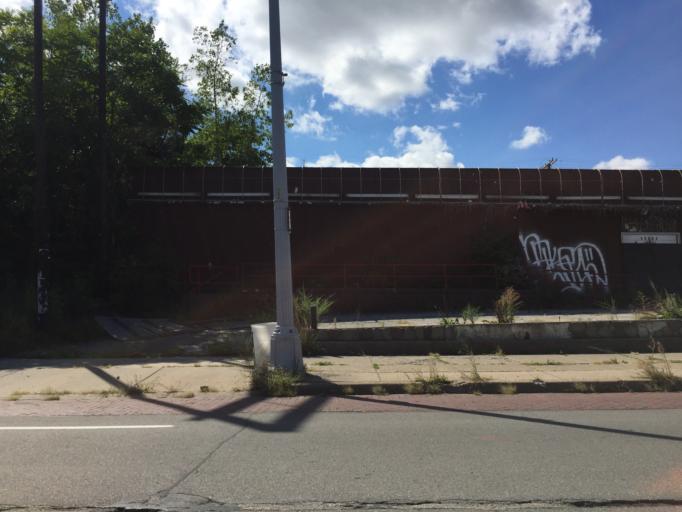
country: US
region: Michigan
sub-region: Wayne County
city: Highland Park
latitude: 42.4117
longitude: -83.1013
